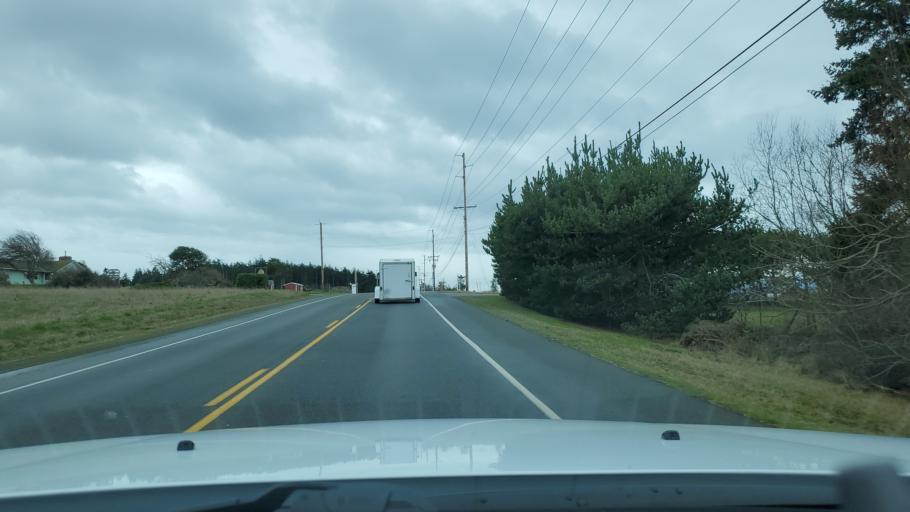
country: US
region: Washington
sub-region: Island County
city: Coupeville
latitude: 48.2435
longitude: -122.7517
